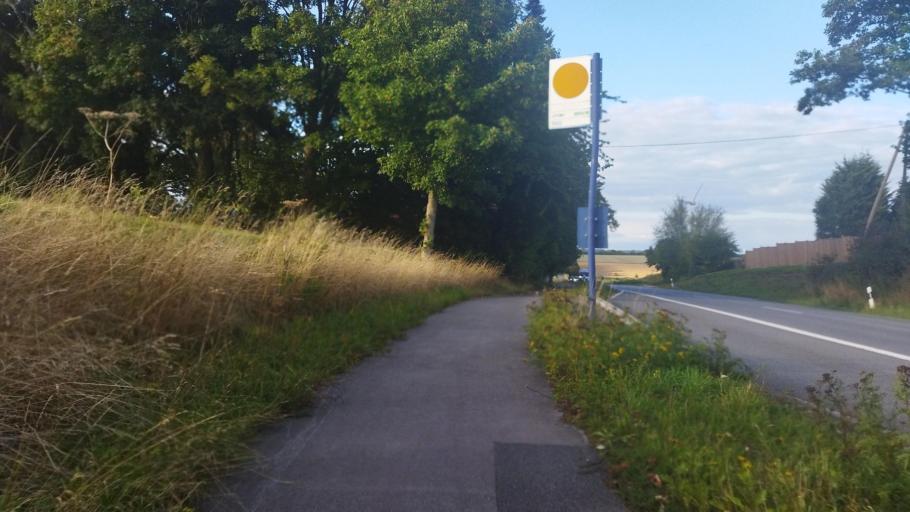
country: DE
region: North Rhine-Westphalia
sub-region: Regierungsbezirk Munster
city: Billerbeck
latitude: 51.9426
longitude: 7.2618
